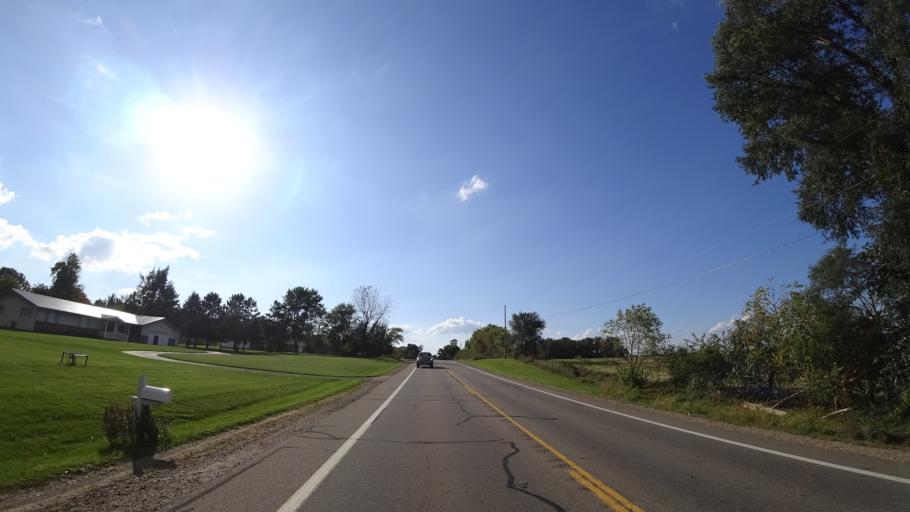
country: US
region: Michigan
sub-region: Saint Joseph County
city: Centreville
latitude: 41.9258
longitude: -85.5620
